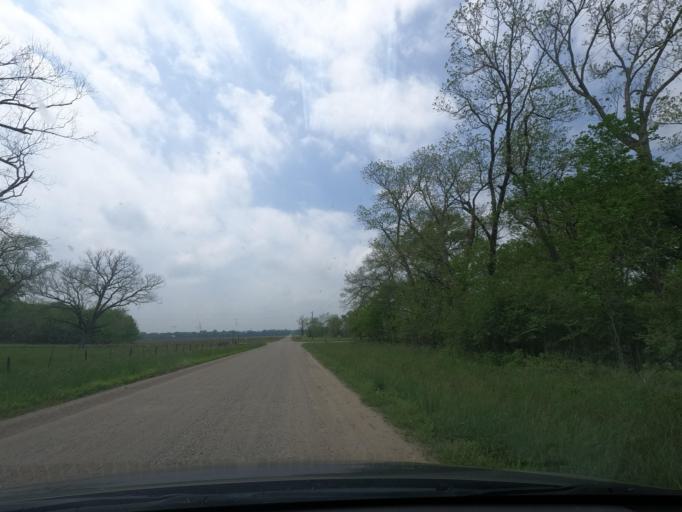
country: US
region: Kansas
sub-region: Labette County
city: Oswego
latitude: 37.2815
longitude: -95.0125
